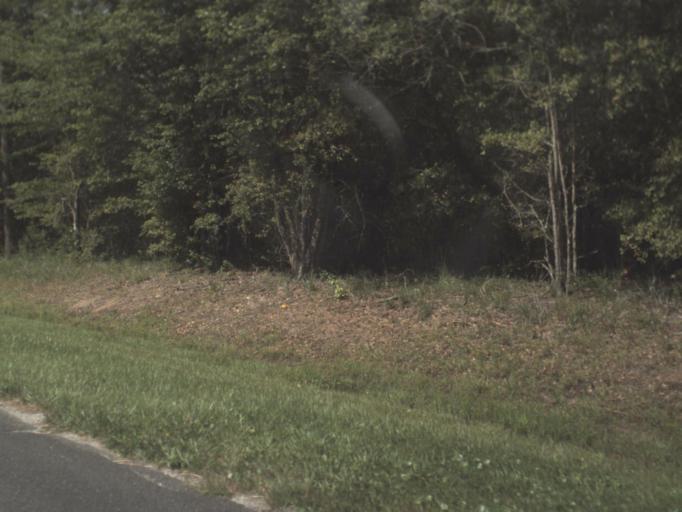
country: US
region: Florida
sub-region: Baker County
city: Macclenny
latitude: 30.2979
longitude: -82.1263
